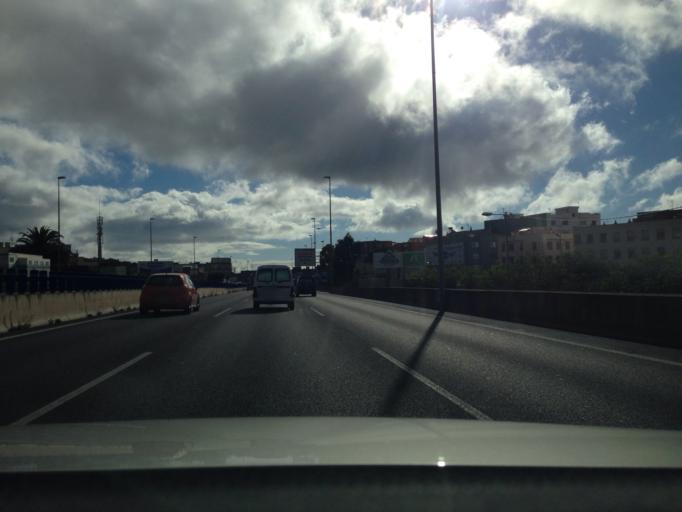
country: ES
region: Canary Islands
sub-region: Provincia de Santa Cruz de Tenerife
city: La Laguna
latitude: 28.4881
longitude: -16.3289
